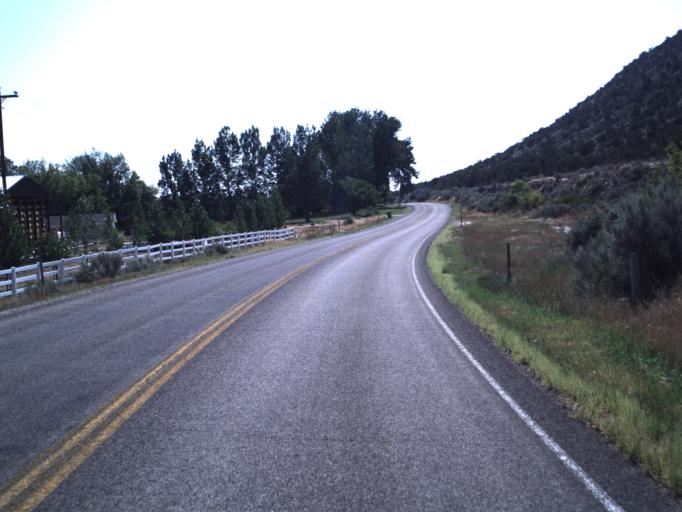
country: US
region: Utah
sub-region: Duchesne County
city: Duchesne
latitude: 40.2822
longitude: -110.4816
